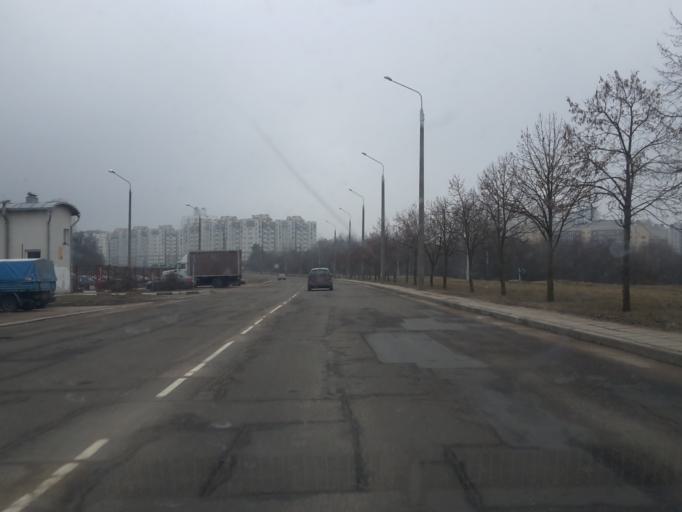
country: BY
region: Minsk
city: Novoye Medvezhino
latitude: 53.8950
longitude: 27.4320
